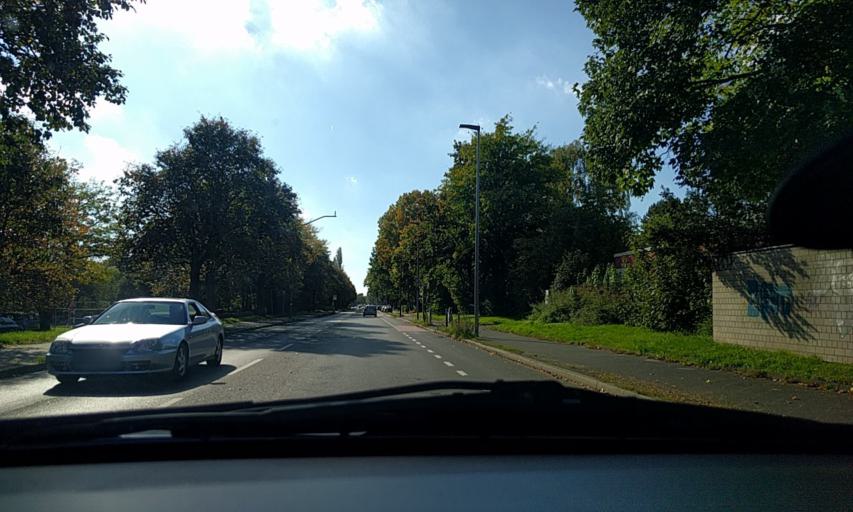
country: DE
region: North Rhine-Westphalia
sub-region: Regierungsbezirk Dusseldorf
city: Dusseldorf
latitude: 51.2562
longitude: 6.8107
